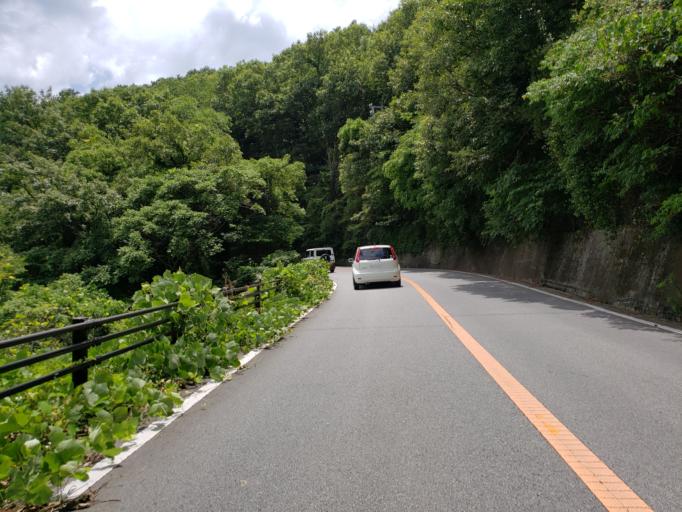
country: JP
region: Hyogo
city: Aioi
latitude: 34.7687
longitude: 134.4916
